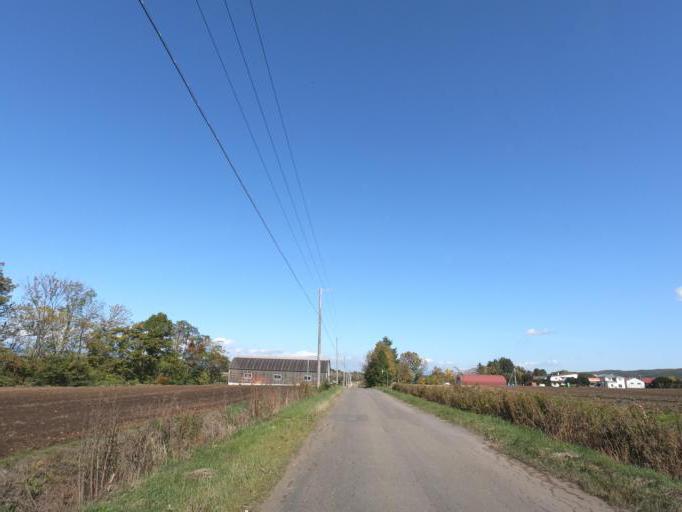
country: JP
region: Hokkaido
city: Otofuke
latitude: 43.0502
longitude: 143.2748
